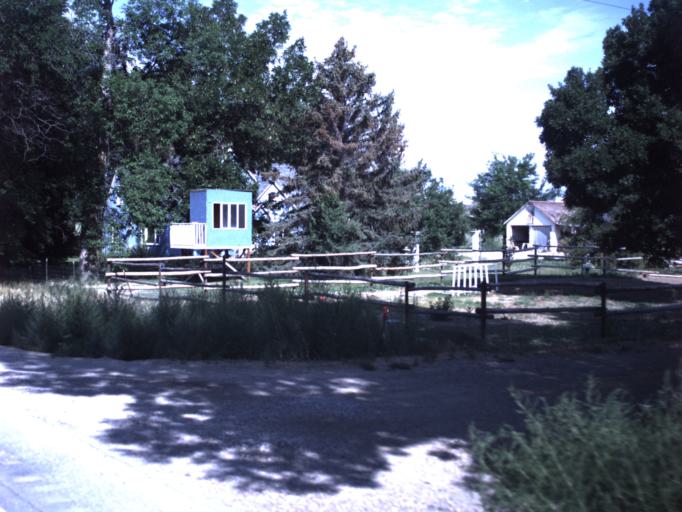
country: US
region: Utah
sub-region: Uintah County
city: Naples
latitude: 40.3697
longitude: -109.3533
